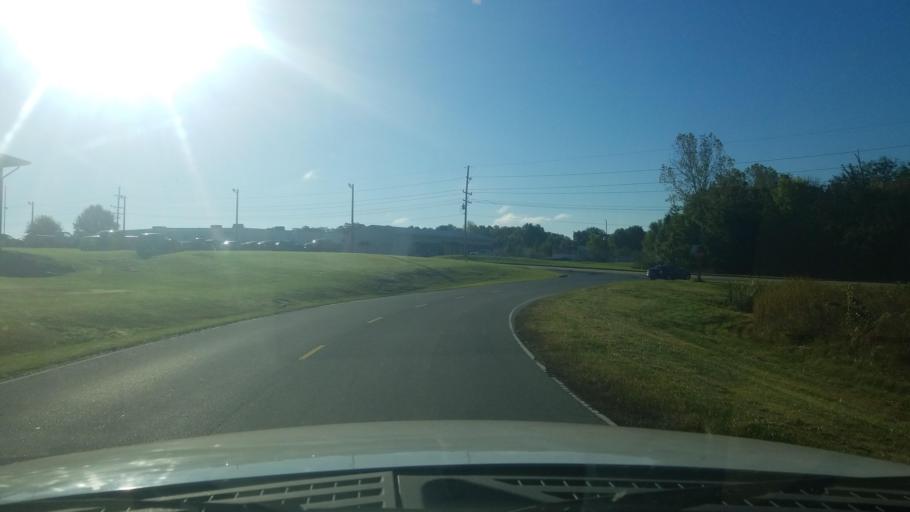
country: US
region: Illinois
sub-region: Williamson County
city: Energy
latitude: 37.7420
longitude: -89.0209
